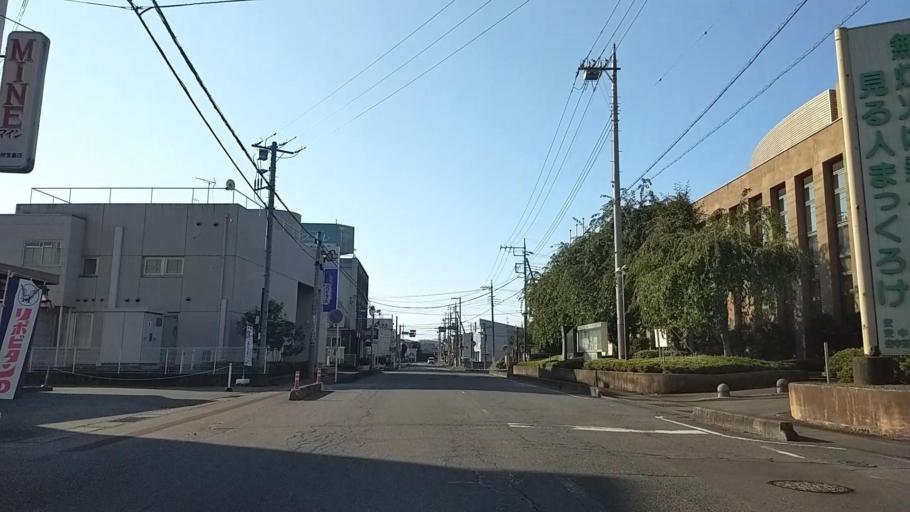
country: JP
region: Gunma
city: Annaka
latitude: 36.3268
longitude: 138.8880
